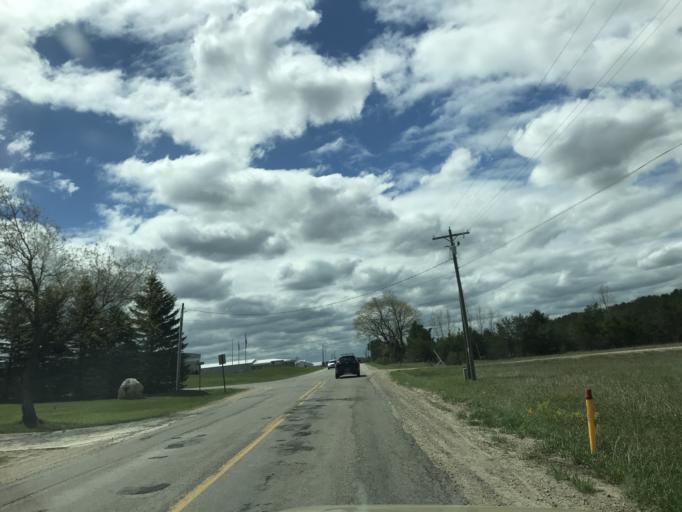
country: US
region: Michigan
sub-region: Otsego County
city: Gaylord
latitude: 45.0349
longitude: -84.6941
